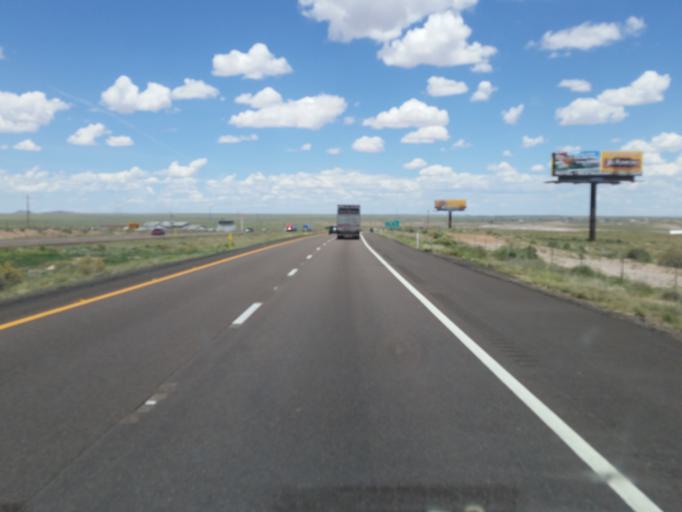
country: US
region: Arizona
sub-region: Navajo County
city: Holbrook
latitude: 34.9685
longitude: -110.0955
